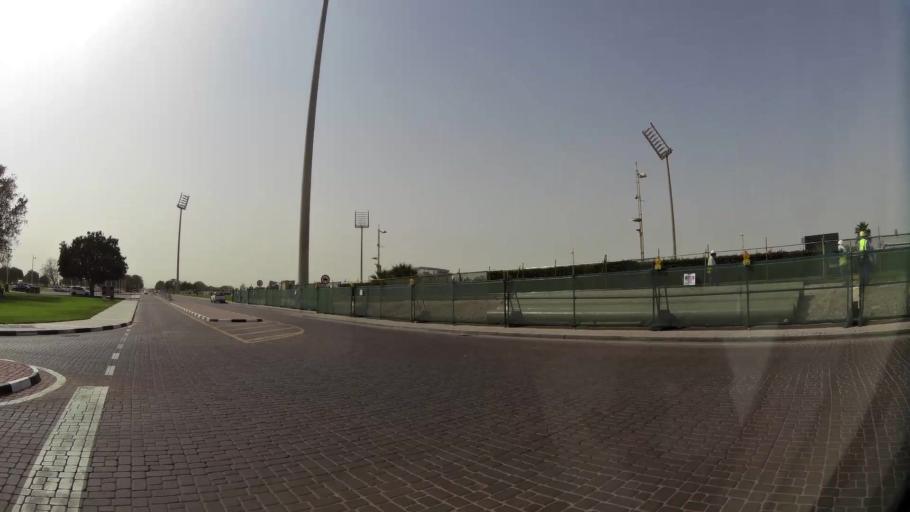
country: QA
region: Baladiyat ar Rayyan
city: Ar Rayyan
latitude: 25.2630
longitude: 51.4403
